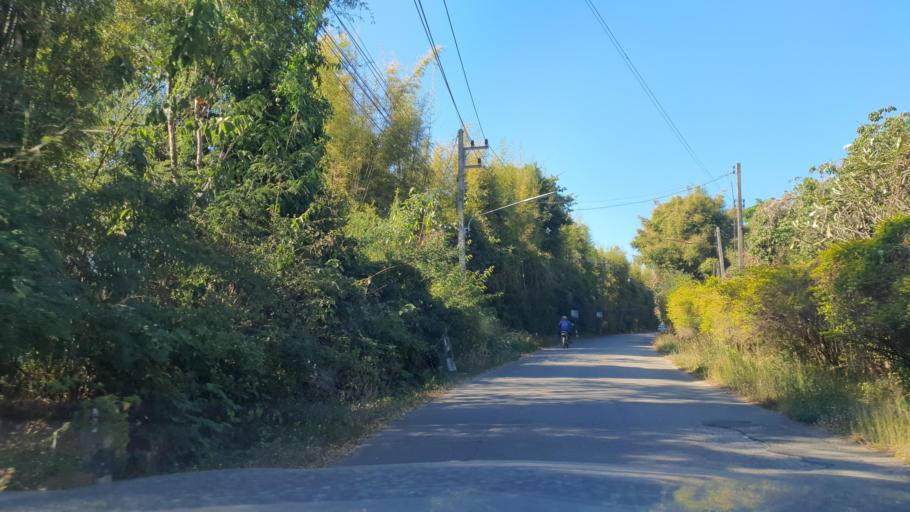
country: TH
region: Chiang Mai
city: Mae Wang
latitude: 18.6824
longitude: 98.8142
